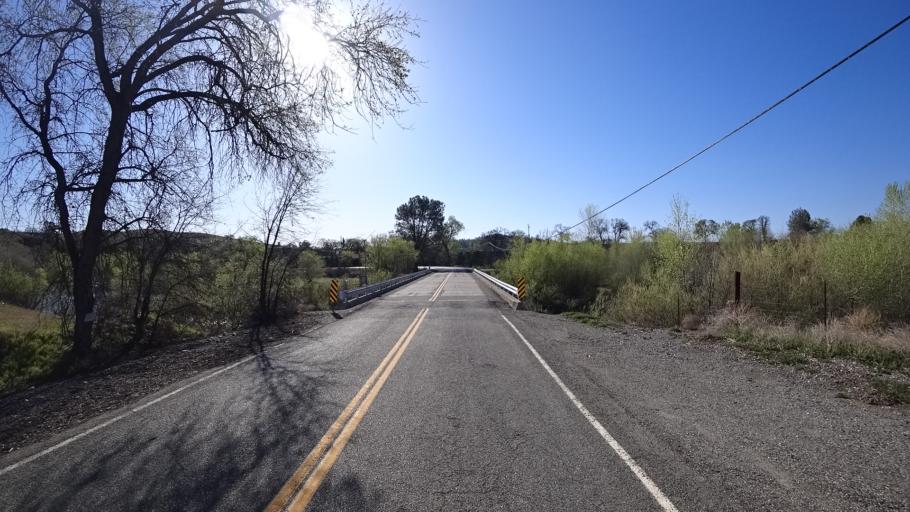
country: US
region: California
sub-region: Glenn County
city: Orland
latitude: 39.6793
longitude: -122.5308
